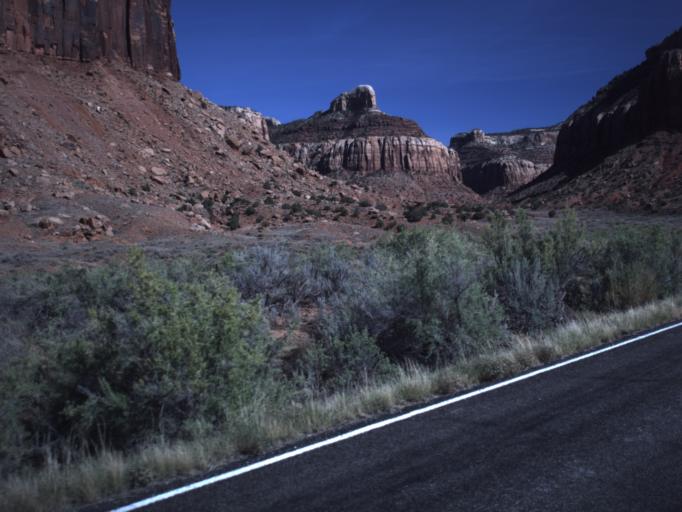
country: US
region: Utah
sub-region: San Juan County
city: Monticello
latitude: 38.0699
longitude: -109.5568
